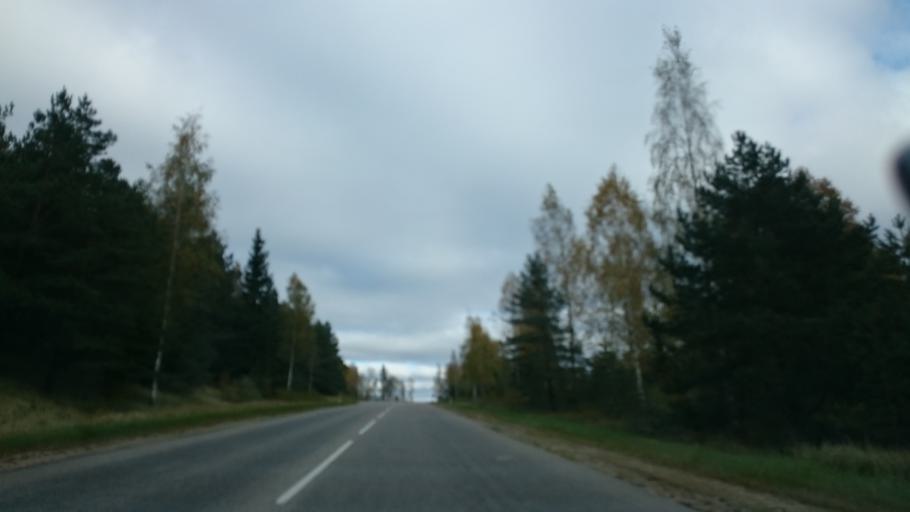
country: LV
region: Amatas Novads
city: Drabesi
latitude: 57.2660
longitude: 25.2720
